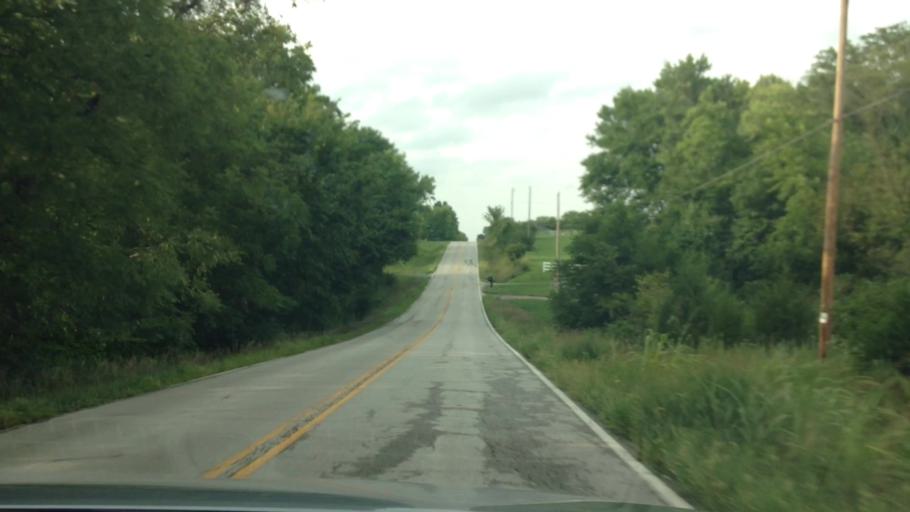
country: US
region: Missouri
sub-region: Clay County
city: Smithville
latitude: 39.3750
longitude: -94.6670
